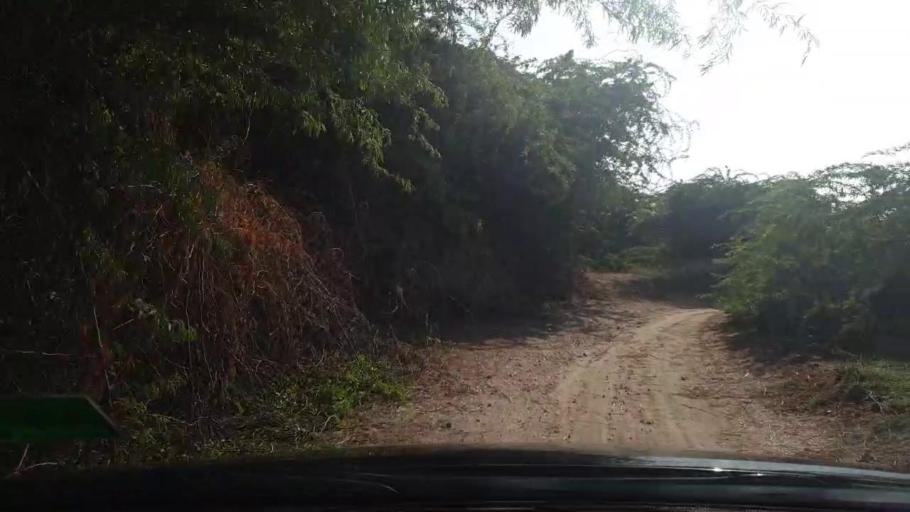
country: PK
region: Sindh
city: Tando Bago
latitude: 24.7148
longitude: 68.9773
